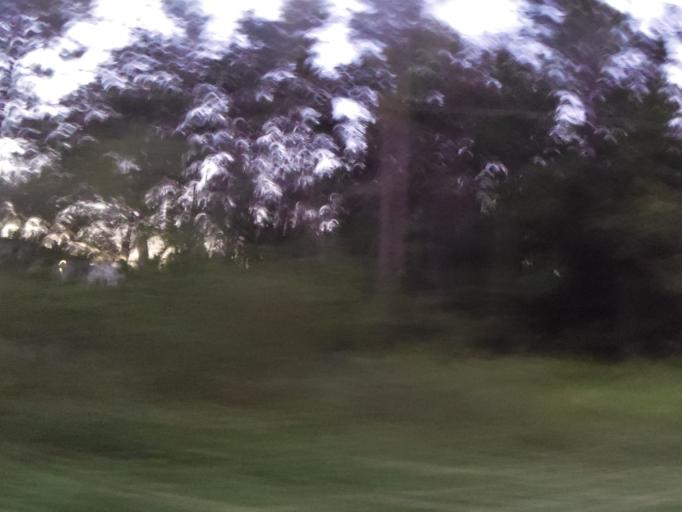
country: US
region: Florida
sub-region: Saint Johns County
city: Palm Valley
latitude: 30.0722
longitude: -81.4895
